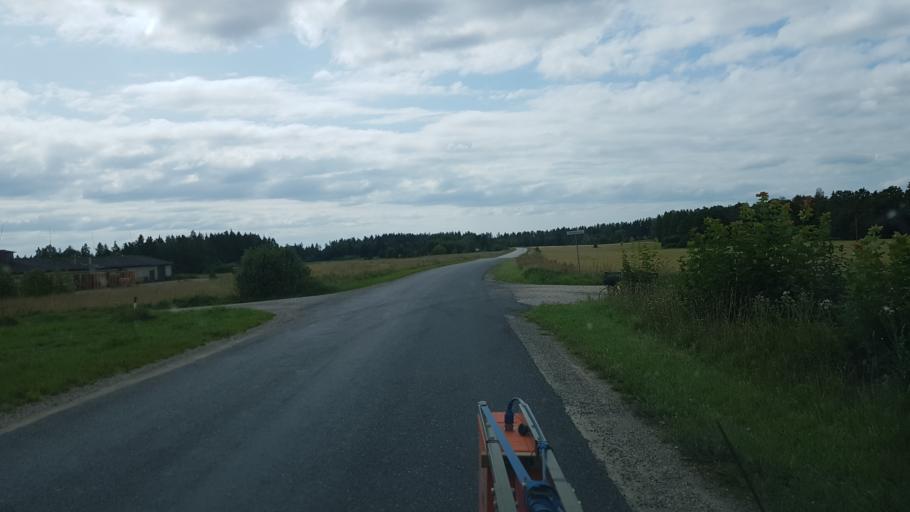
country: EE
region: Paernumaa
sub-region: Halinga vald
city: Parnu-Jaagupi
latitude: 58.5865
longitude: 24.4068
